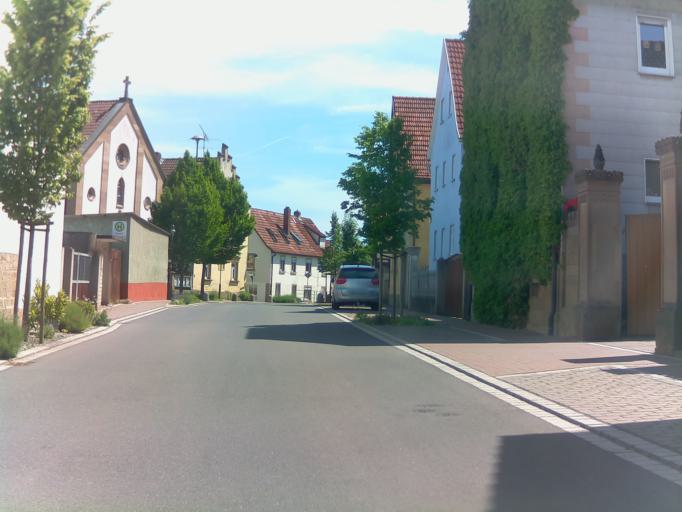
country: DE
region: Bavaria
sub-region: Regierungsbezirk Unterfranken
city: Poppenhausen
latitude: 50.0842
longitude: 10.1446
